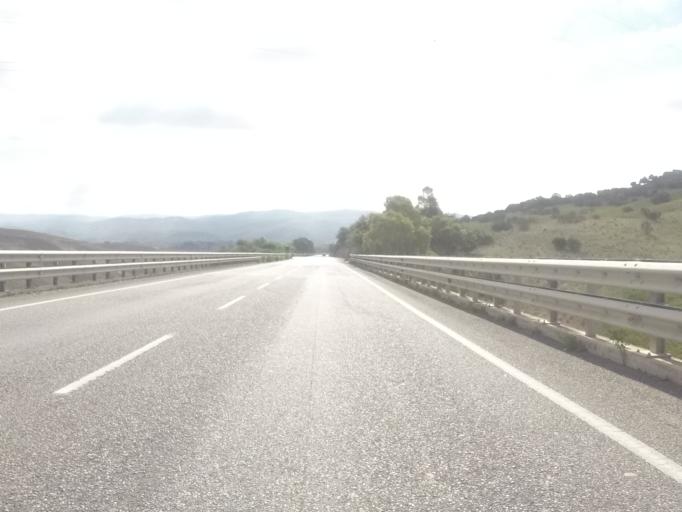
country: IT
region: Sicily
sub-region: Provincia di Caltanissetta
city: Caltanissetta
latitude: 37.4736
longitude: 14.0903
